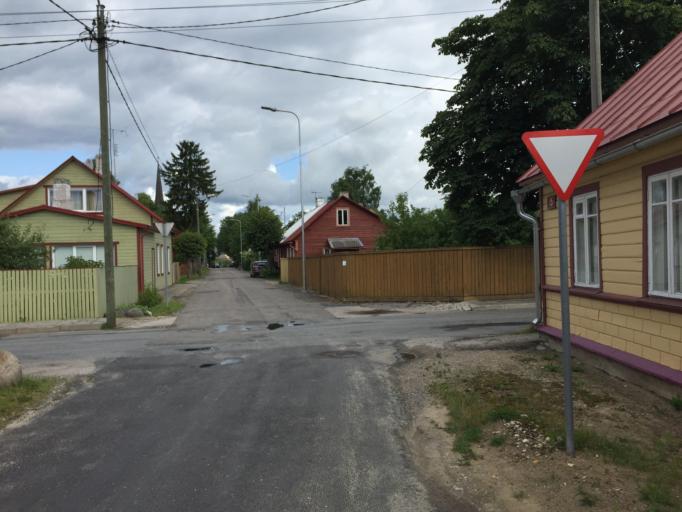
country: EE
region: Laeaene
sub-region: Haapsalu linn
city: Haapsalu
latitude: 58.9426
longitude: 23.5368
